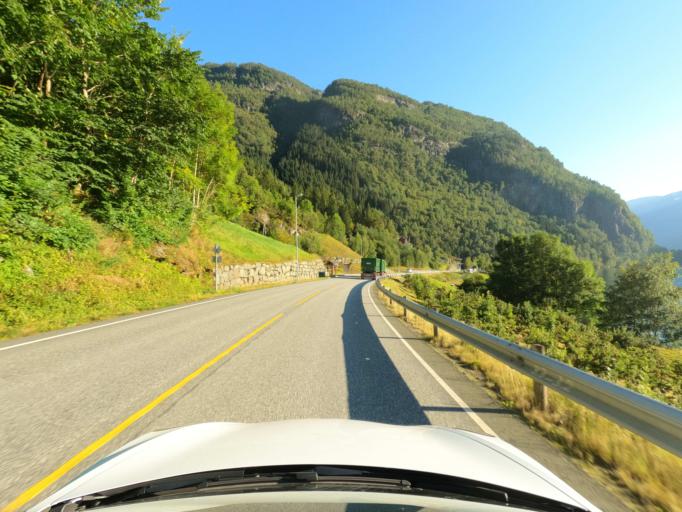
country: NO
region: Hordaland
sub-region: Odda
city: Odda
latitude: 60.1865
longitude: 6.5896
